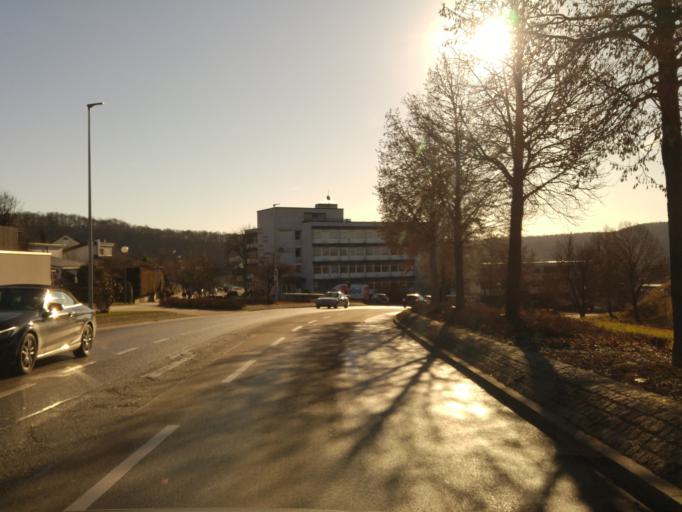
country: DE
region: Baden-Wuerttemberg
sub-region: Regierungsbezirk Stuttgart
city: Leonberg
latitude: 48.7926
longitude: 9.0186
